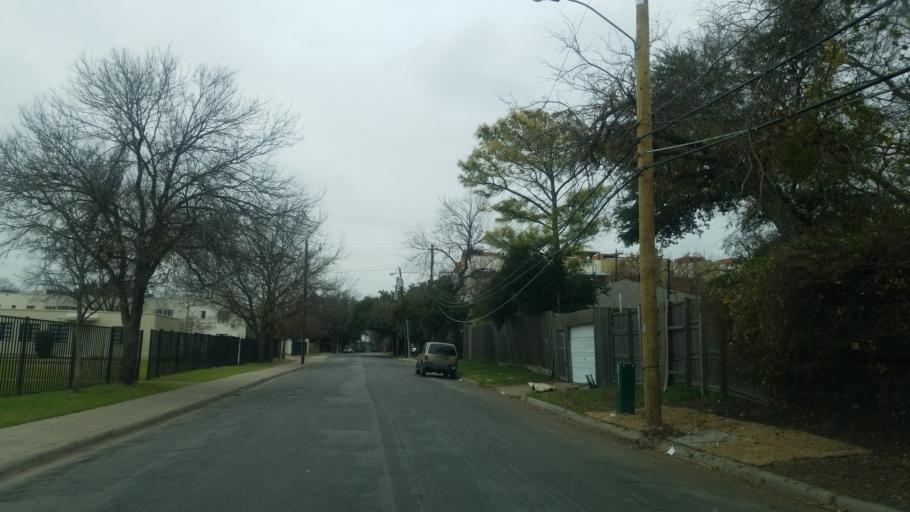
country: US
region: Texas
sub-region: Dallas County
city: Highland Park
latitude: 32.8150
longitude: -96.8194
